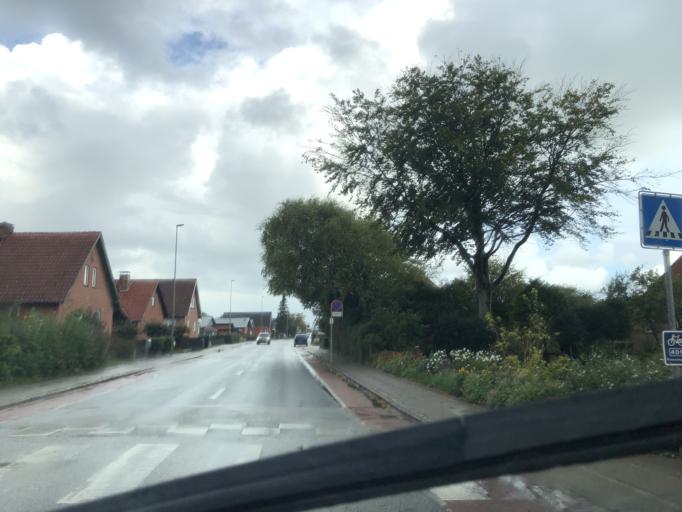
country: DK
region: Central Jutland
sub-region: Lemvig Kommune
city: Lemvig
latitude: 56.5475
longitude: 8.2932
